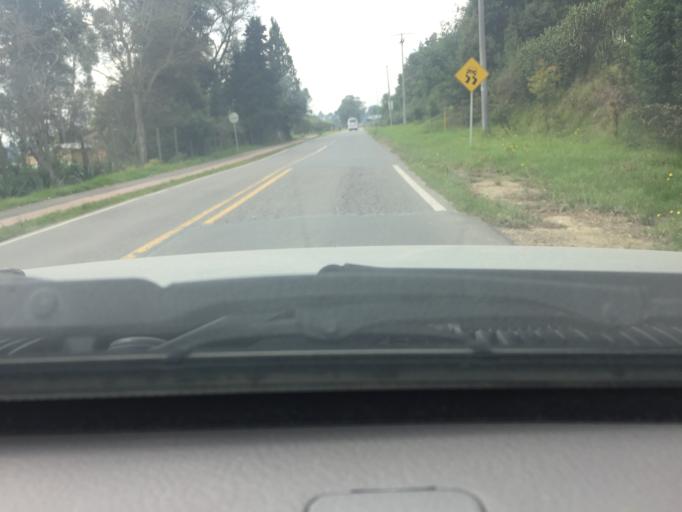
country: CO
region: Cundinamarca
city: Bojaca
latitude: 4.7565
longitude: -74.3343
